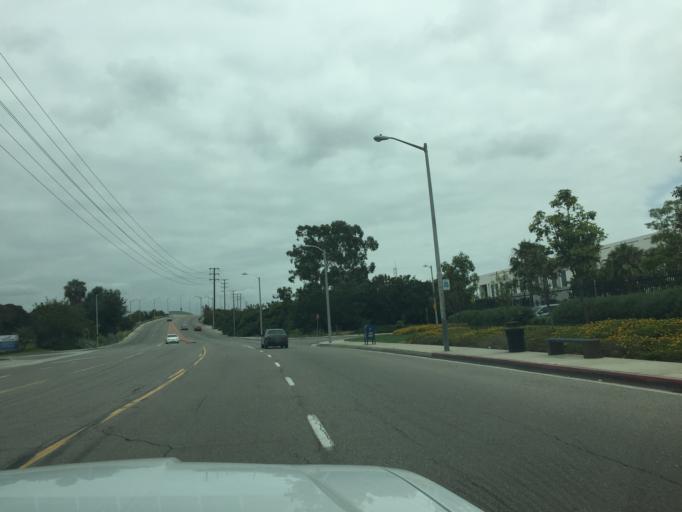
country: US
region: California
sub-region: Los Angeles County
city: Carson
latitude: 33.8317
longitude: -118.2302
